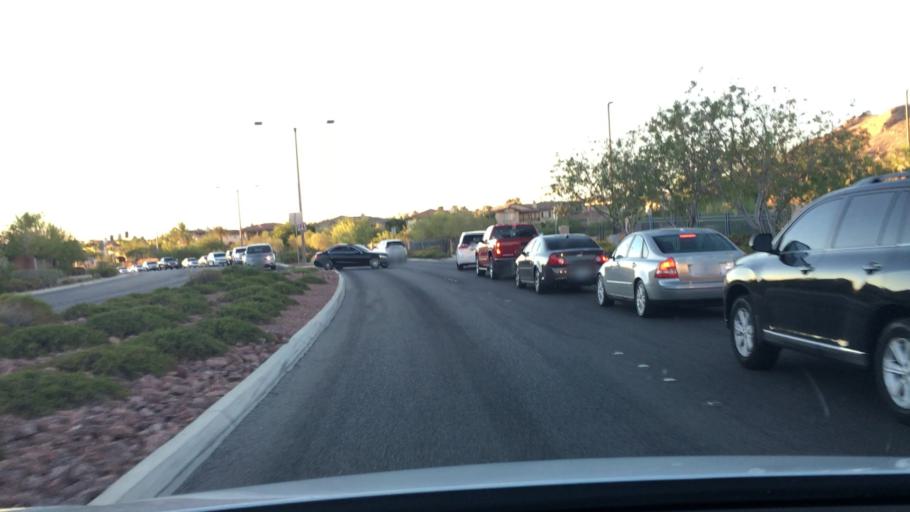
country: US
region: Nevada
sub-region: Clark County
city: Summerlin South
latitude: 36.1576
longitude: -115.3520
